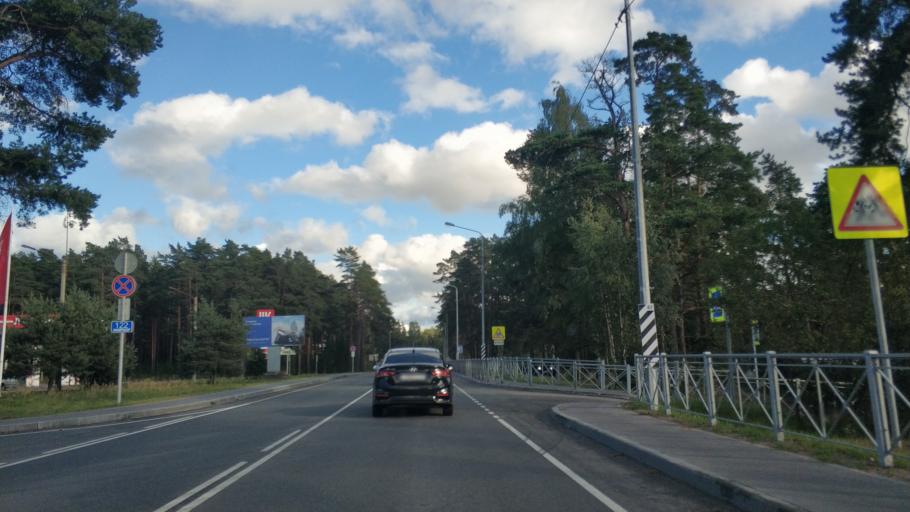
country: RU
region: Leningrad
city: Priozersk
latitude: 61.0192
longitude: 30.1347
